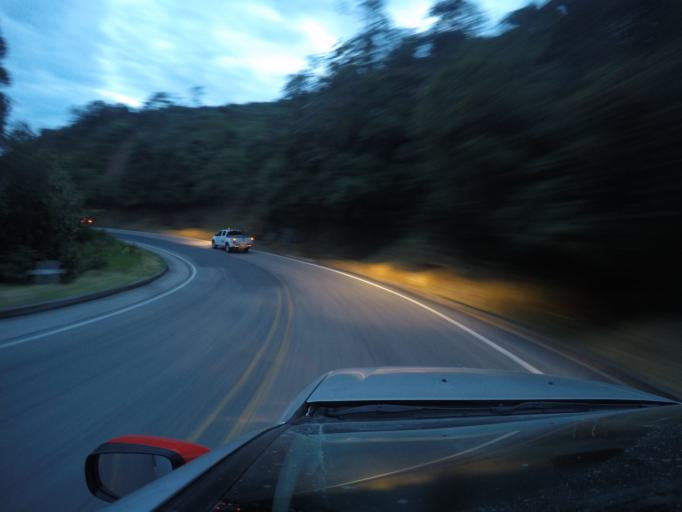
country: CO
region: Tolima
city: Herveo
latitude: 5.1384
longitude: -75.1447
